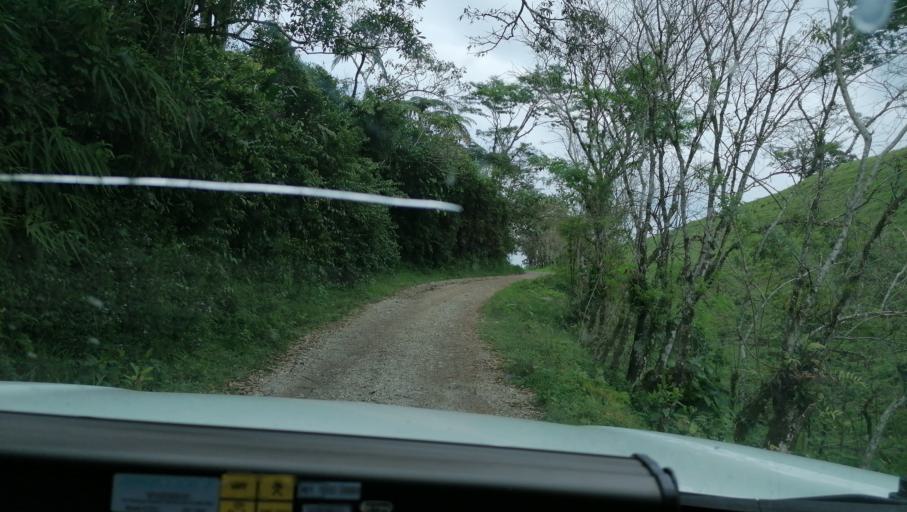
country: MX
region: Chiapas
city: Ocotepec
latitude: 17.3240
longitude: -93.1342
